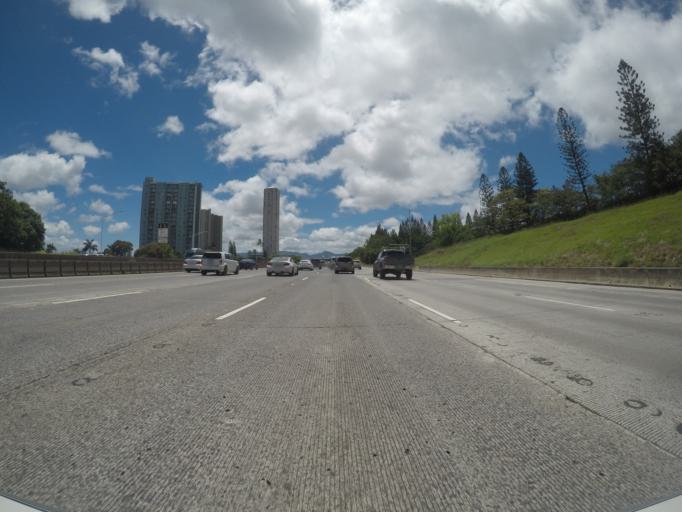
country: US
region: Hawaii
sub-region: Honolulu County
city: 'Aiea
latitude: 21.3874
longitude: -157.9374
